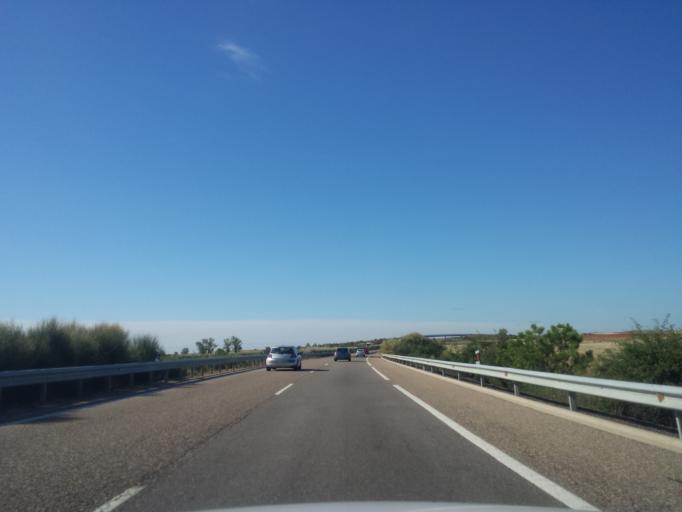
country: ES
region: Castille and Leon
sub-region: Provincia de Zamora
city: Matilla de Arzon
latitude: 42.0812
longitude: -5.6555
